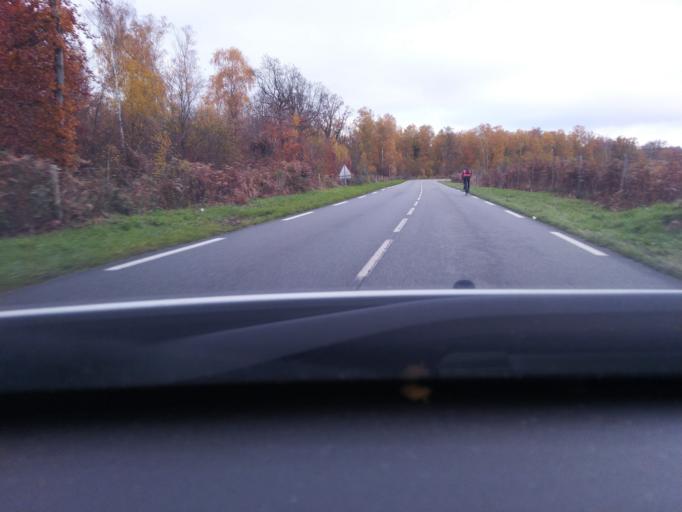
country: FR
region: Haute-Normandie
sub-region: Departement de la Seine-Maritime
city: Duclair
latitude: 49.4922
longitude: 0.8973
